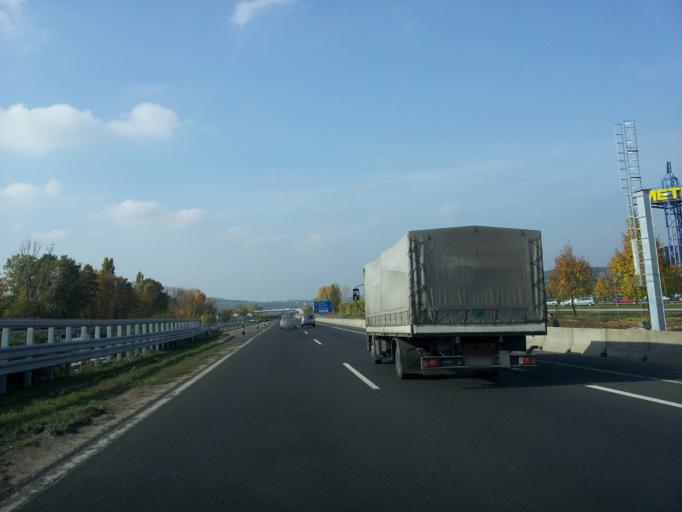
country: HU
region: Pest
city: Toeroekbalint
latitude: 47.4560
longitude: 18.8999
